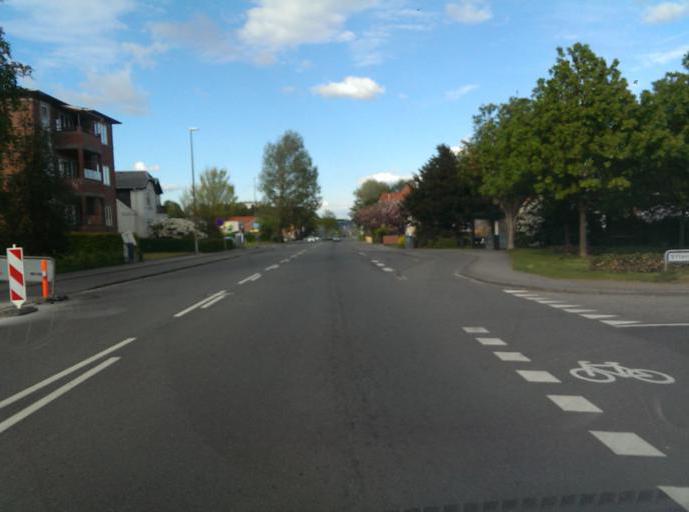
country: DK
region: South Denmark
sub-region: Esbjerg Kommune
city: Esbjerg
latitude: 55.4768
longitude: 8.4858
